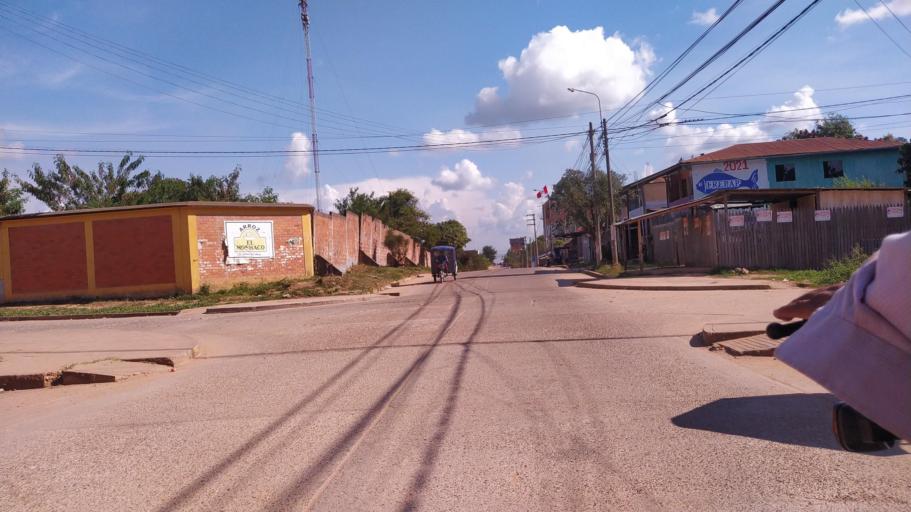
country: PE
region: Ucayali
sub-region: Provincia de Coronel Portillo
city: Puerto Callao
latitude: -8.3551
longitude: -74.5793
